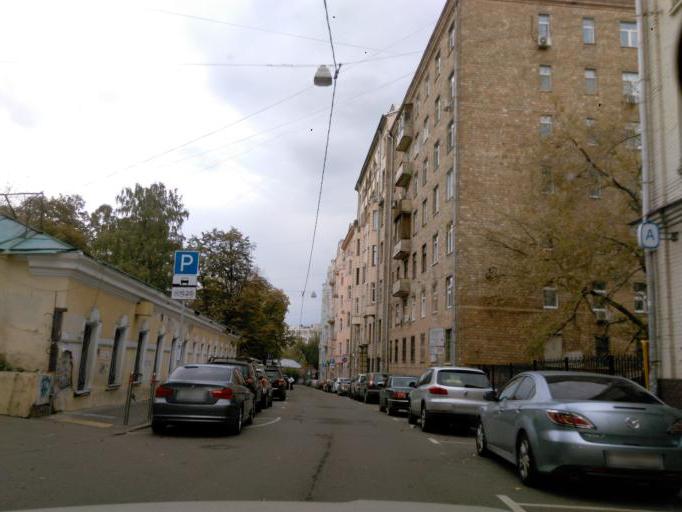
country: RU
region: Moscow
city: Taganskiy
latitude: 55.7603
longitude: 37.6527
